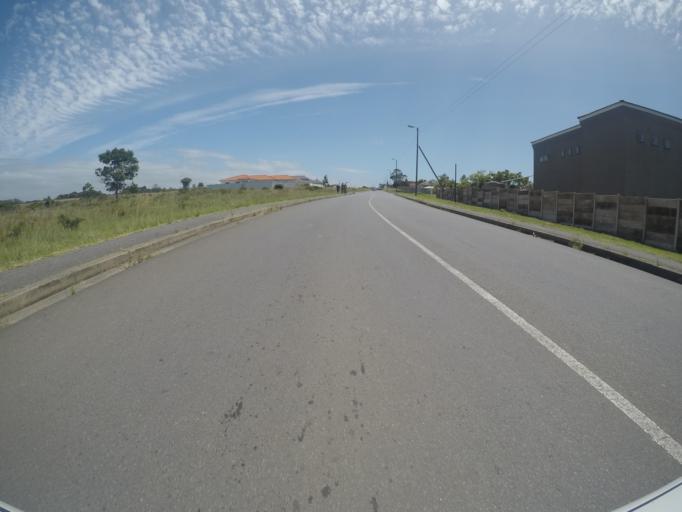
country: ZA
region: Eastern Cape
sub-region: Buffalo City Metropolitan Municipality
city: East London
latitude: -32.9431
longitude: 27.9935
